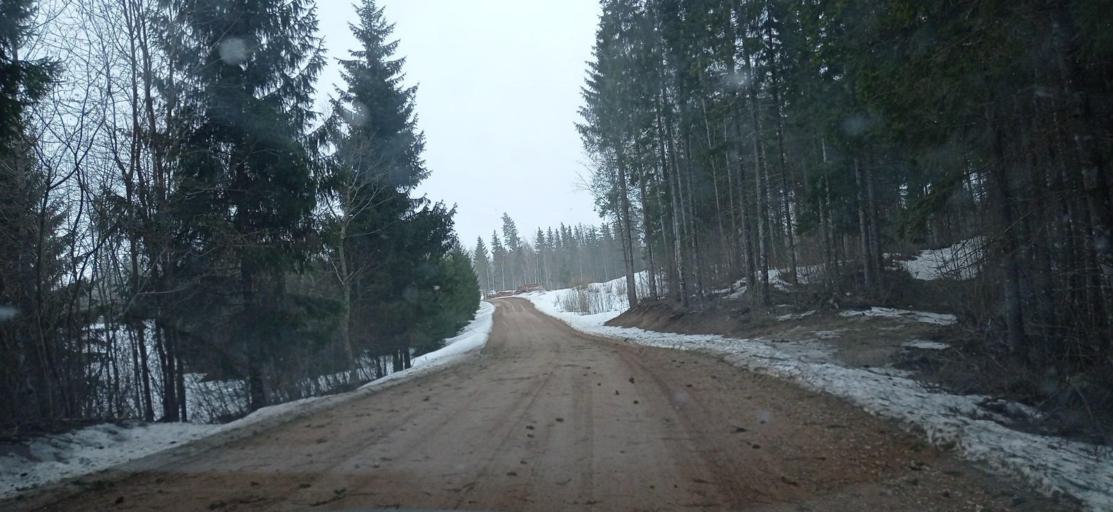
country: EE
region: Tartu
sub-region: UElenurme vald
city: Ulenurme
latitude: 58.1190
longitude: 26.7002
